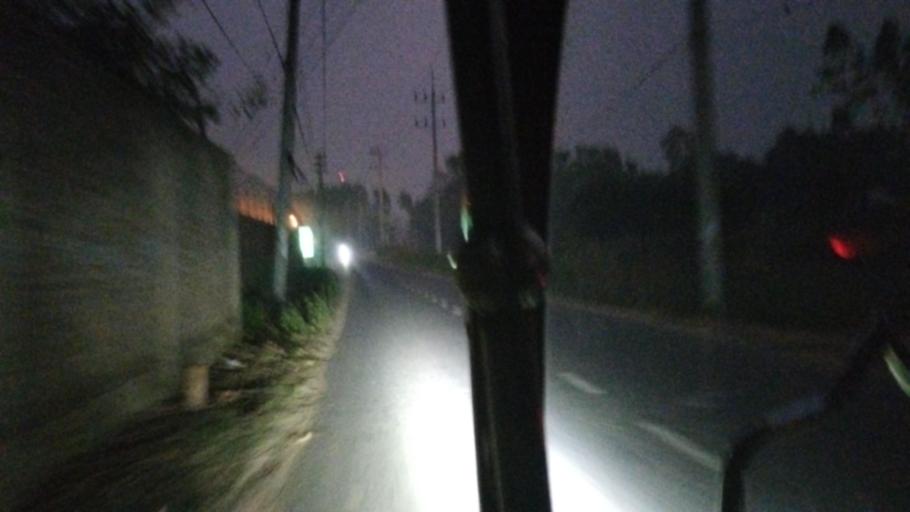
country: BD
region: Dhaka
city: Sakhipur
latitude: 24.4017
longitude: 90.3536
